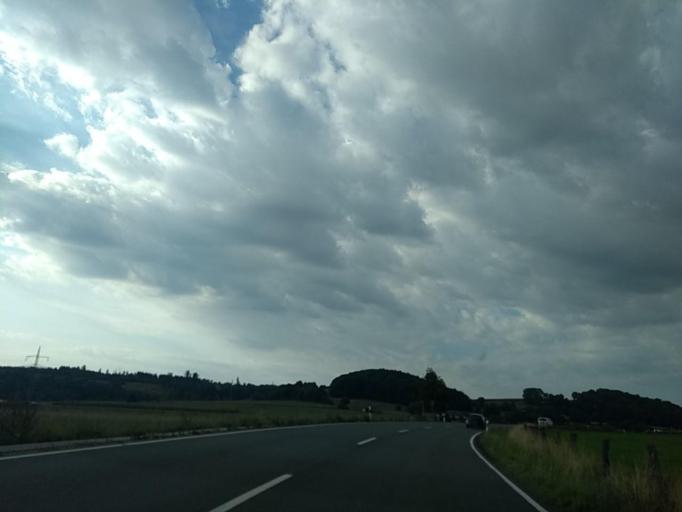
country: DE
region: North Rhine-Westphalia
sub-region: Regierungsbezirk Detmold
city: Wunnenberg
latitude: 51.4663
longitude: 8.6381
